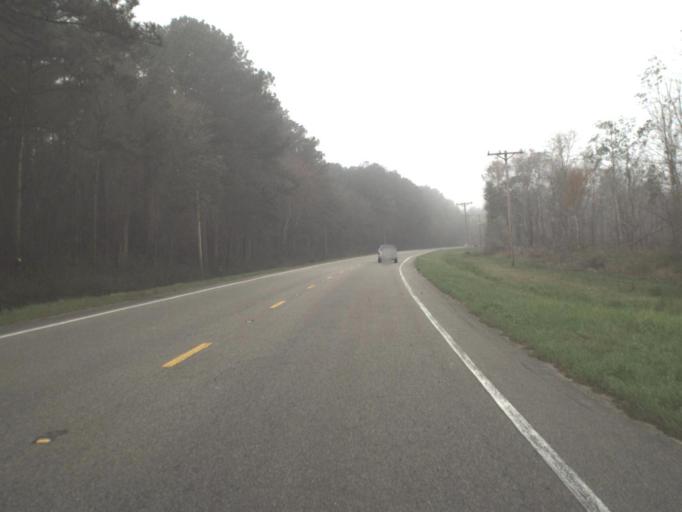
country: US
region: Florida
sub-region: Gadsden County
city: Gretna
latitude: 30.5192
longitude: -84.6937
